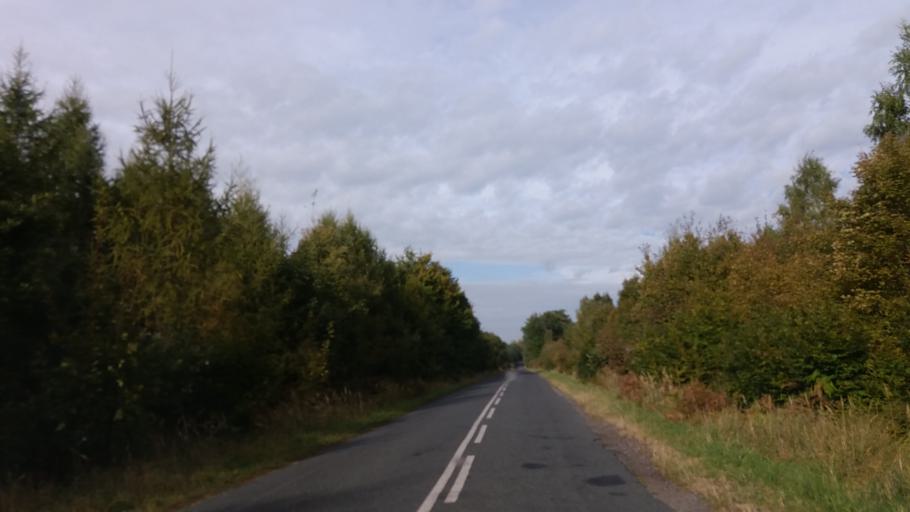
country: PL
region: West Pomeranian Voivodeship
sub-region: Powiat choszczenski
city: Krzecin
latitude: 53.0044
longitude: 15.5004
